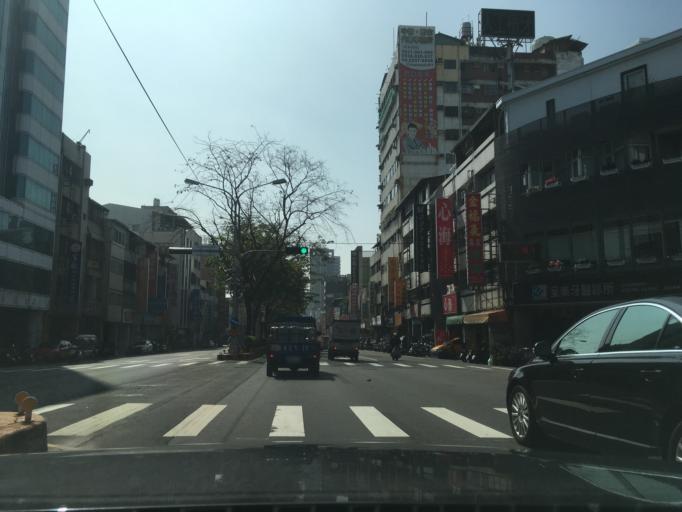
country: TW
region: Taiwan
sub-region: Taichung City
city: Taichung
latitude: 24.1620
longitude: 120.6749
